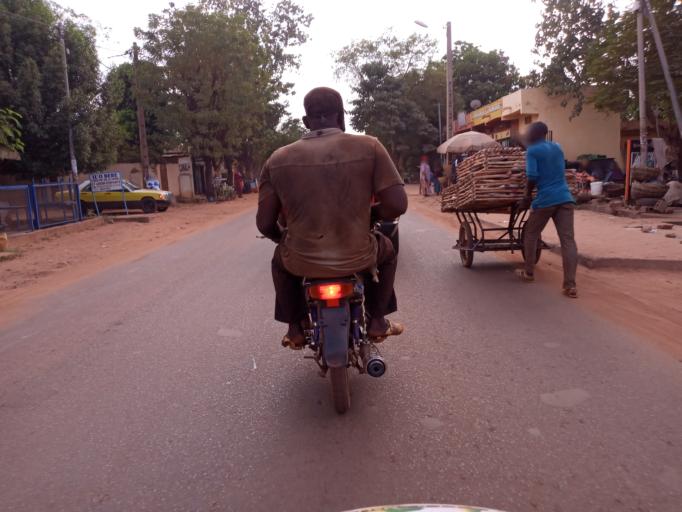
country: ML
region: Bamako
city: Bamako
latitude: 12.5882
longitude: -7.9498
